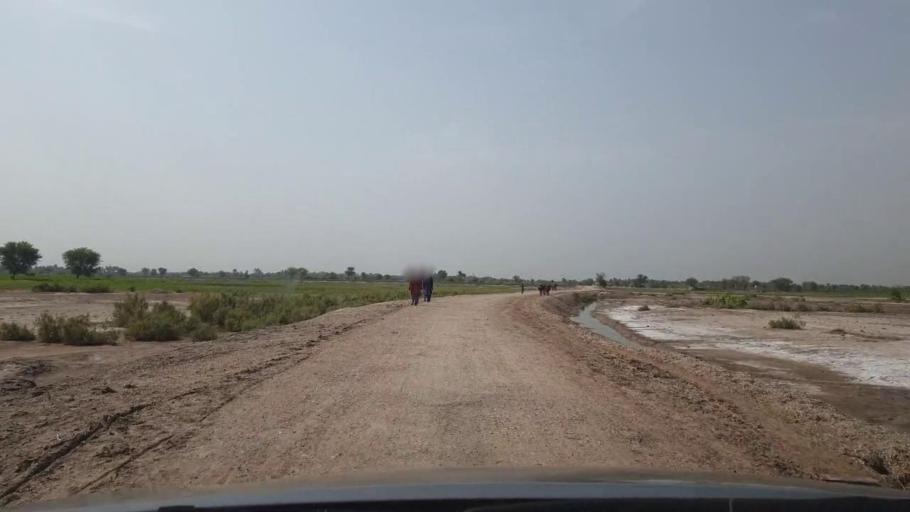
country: PK
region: Sindh
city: Rohri
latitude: 27.6691
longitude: 69.0137
